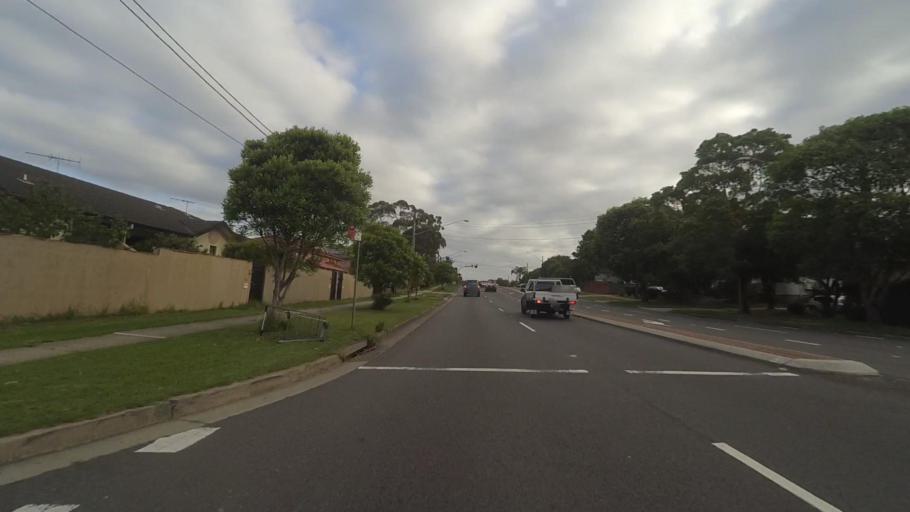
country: AU
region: New South Wales
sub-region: Bankstown
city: Padstow
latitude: -33.9527
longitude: 151.0383
